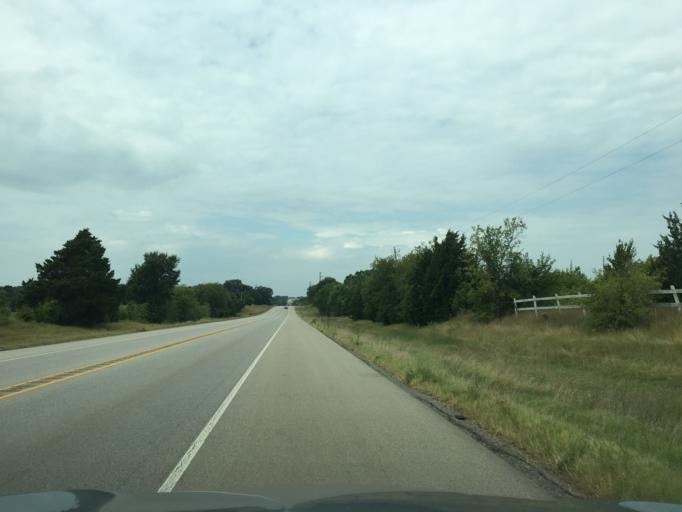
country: US
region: Texas
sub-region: Collin County
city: Anna
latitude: 33.3261
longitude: -96.4917
